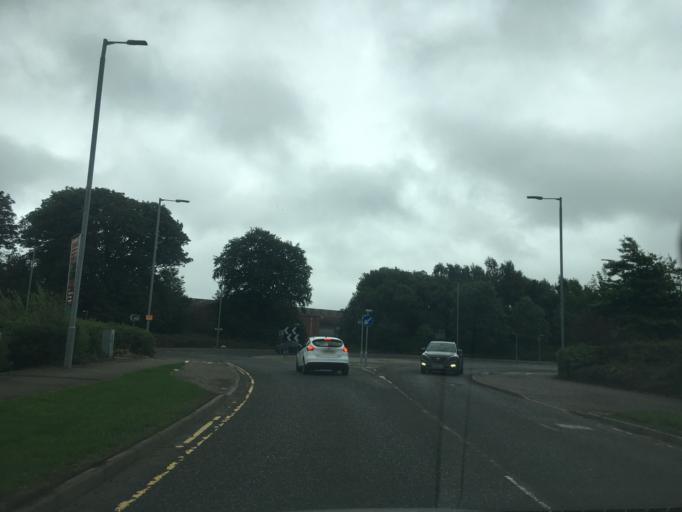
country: GB
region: Scotland
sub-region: Renfrewshire
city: Renfrew
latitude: 55.8713
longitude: -4.3570
